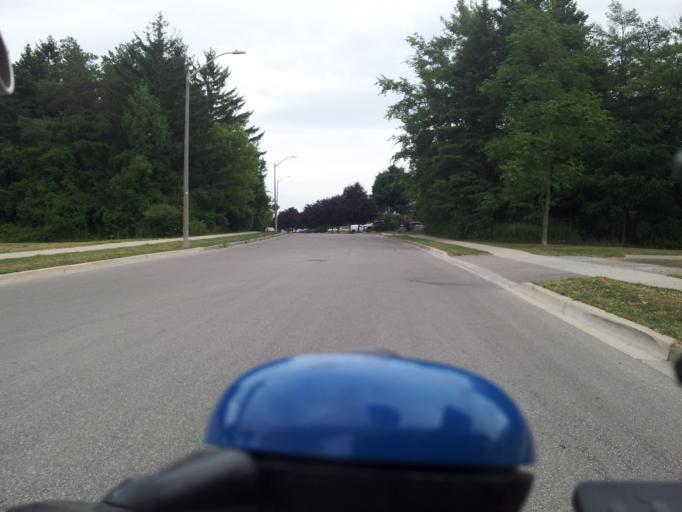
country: CA
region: Ontario
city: Stratford
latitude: 43.3554
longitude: -80.9896
